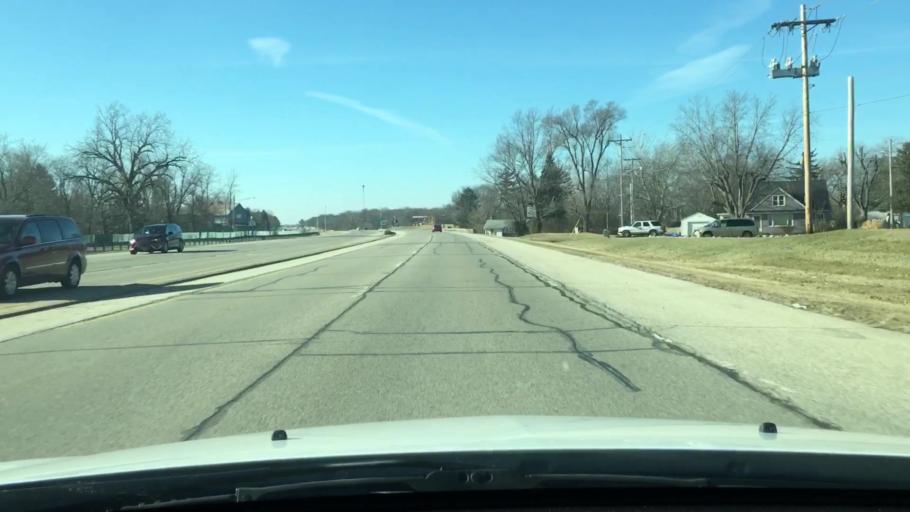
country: US
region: Illinois
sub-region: Woodford County
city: Germantown Hills
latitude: 40.7666
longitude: -89.4671
